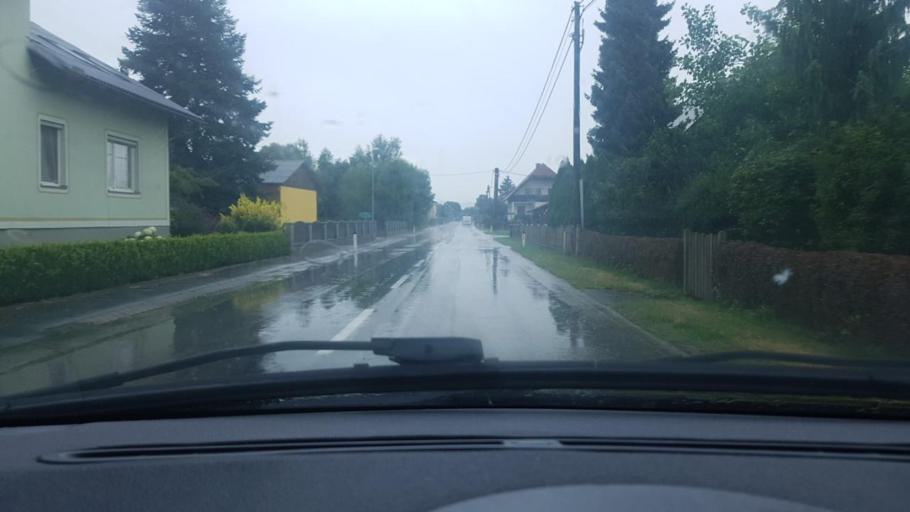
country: AT
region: Styria
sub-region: Politischer Bezirk Graz-Umgebung
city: Zettling
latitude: 46.9562
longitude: 15.4296
